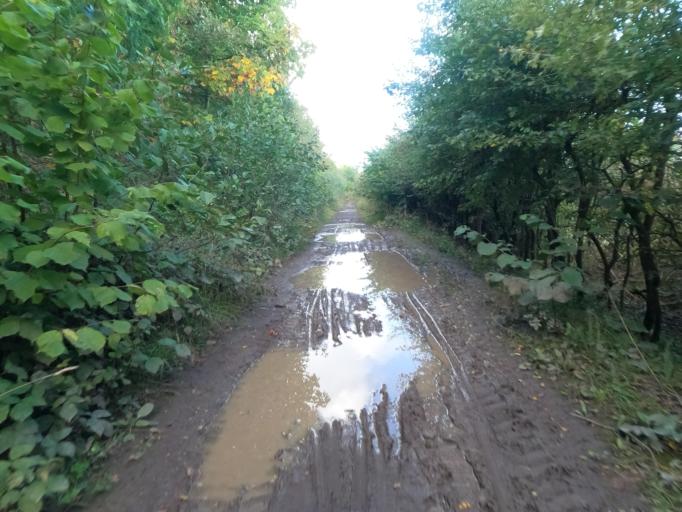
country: GB
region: England
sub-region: Northumberland
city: Seghill
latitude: 55.0722
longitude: -1.5483
